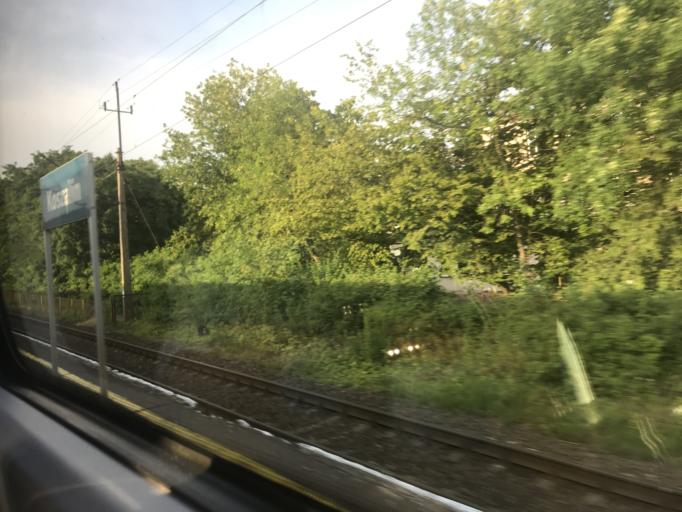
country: PL
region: West Pomeranian Voivodeship
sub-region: Koszalin
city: Koszalin
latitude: 54.1890
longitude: 16.1692
